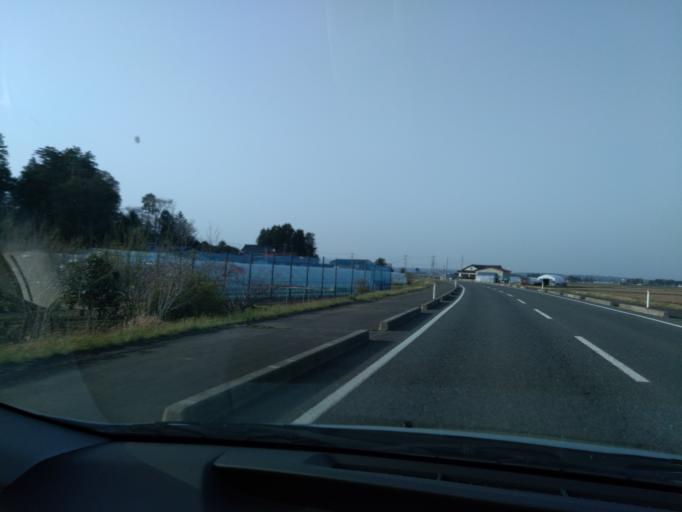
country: JP
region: Iwate
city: Ichinoseki
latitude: 38.7414
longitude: 141.1309
